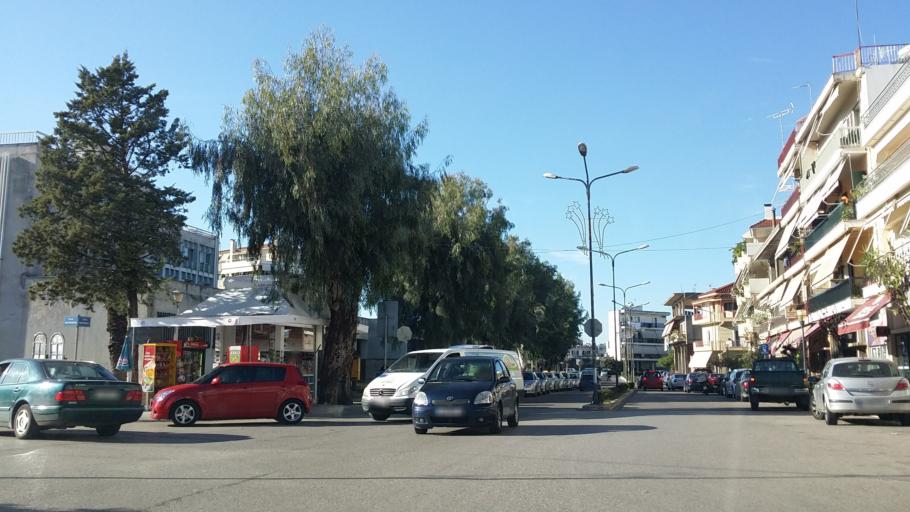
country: GR
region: West Greece
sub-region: Nomos Aitolias kai Akarnanias
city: Agrinio
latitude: 38.6225
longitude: 21.4033
